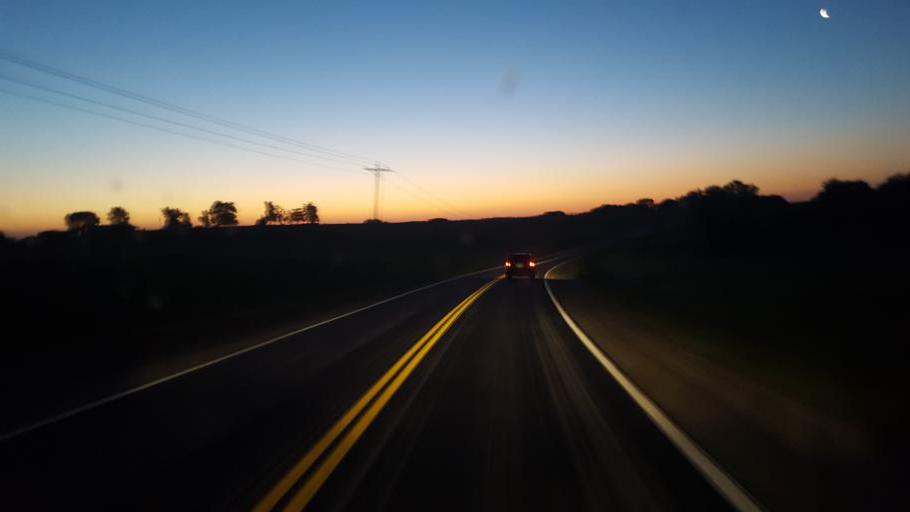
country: US
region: Missouri
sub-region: Mercer County
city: Princeton
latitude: 40.4109
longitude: -93.5449
